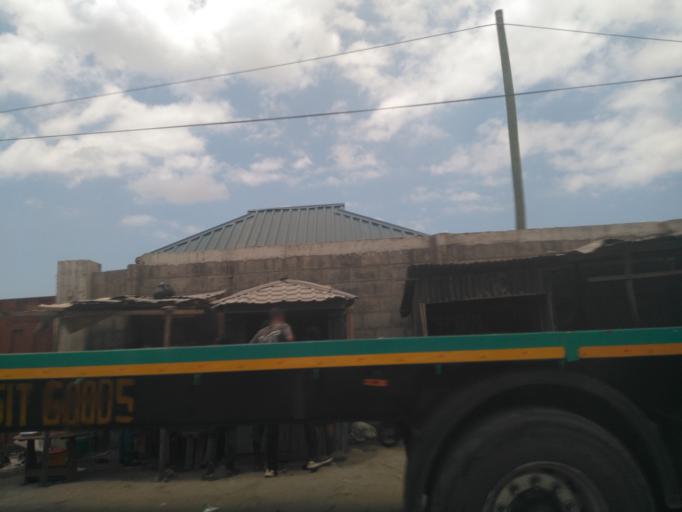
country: TZ
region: Dar es Salaam
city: Dar es Salaam
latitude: -6.8621
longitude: 39.2787
